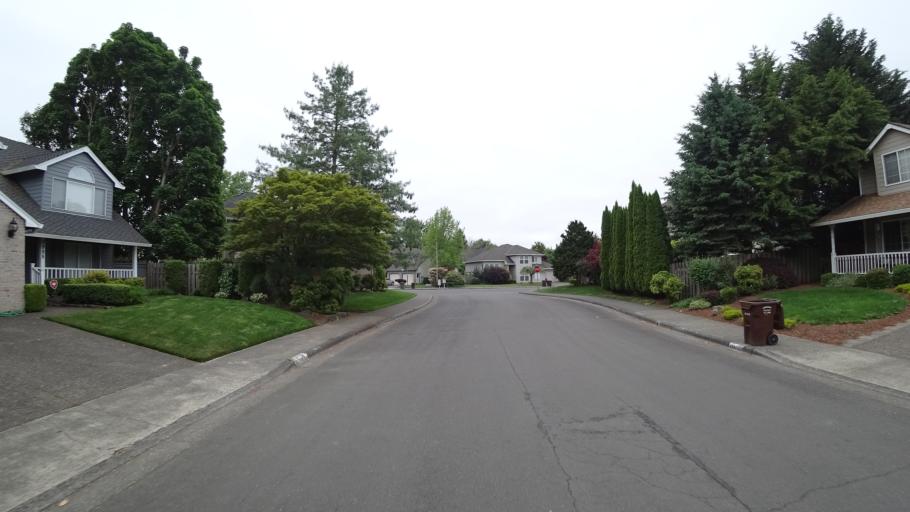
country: US
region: Oregon
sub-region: Washington County
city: Bethany
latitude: 45.5484
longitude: -122.8589
